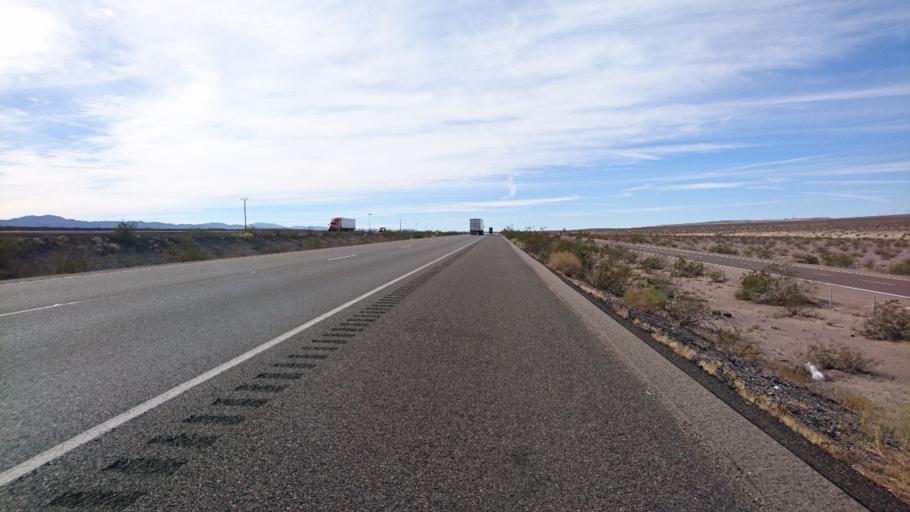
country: US
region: California
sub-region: San Bernardino County
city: Joshua Tree
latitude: 34.7276
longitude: -116.2510
